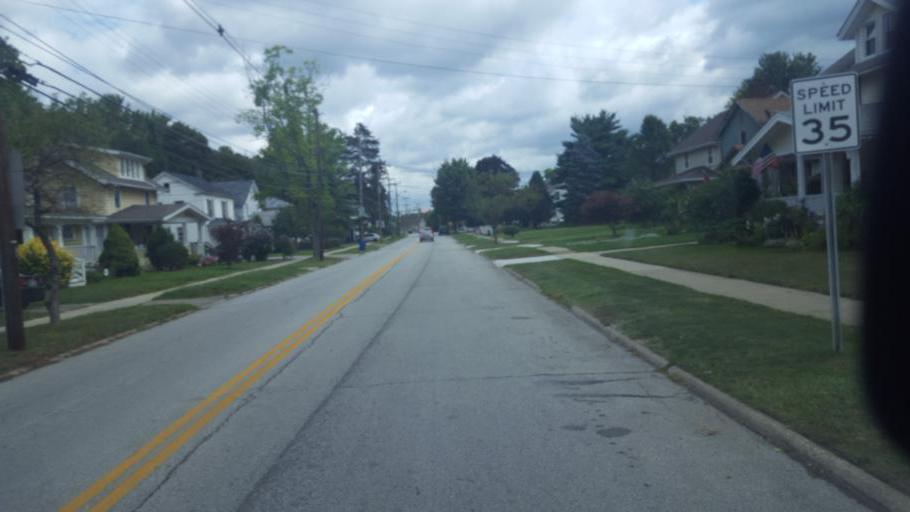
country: US
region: Ohio
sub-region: Lake County
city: Painesville
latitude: 41.7190
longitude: -81.2348
